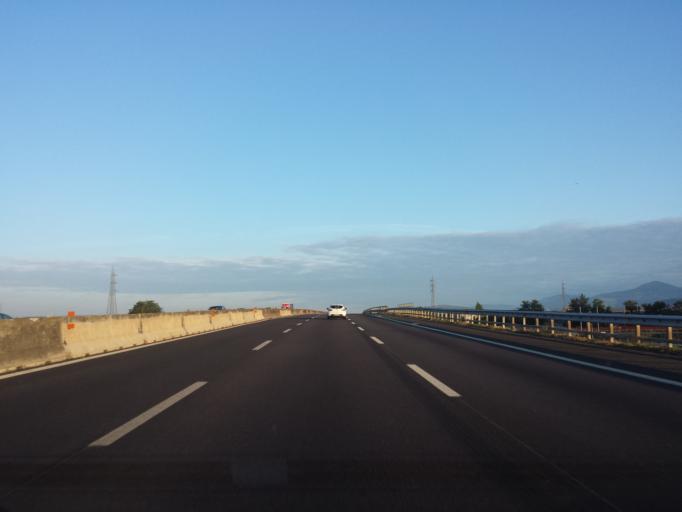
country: IT
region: Lombardy
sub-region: Provincia di Brescia
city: Castegnato
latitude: 45.5464
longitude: 10.1208
